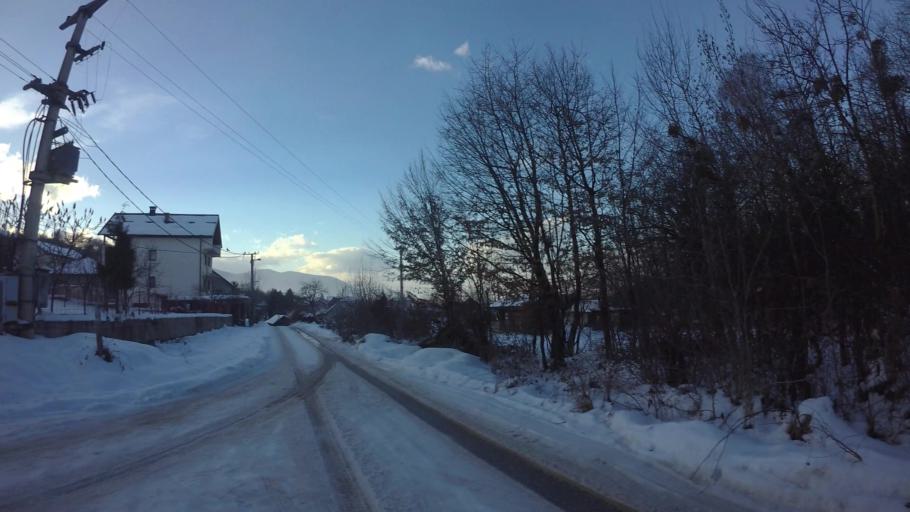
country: BA
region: Federation of Bosnia and Herzegovina
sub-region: Kanton Sarajevo
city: Sarajevo
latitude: 43.8078
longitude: 18.3597
